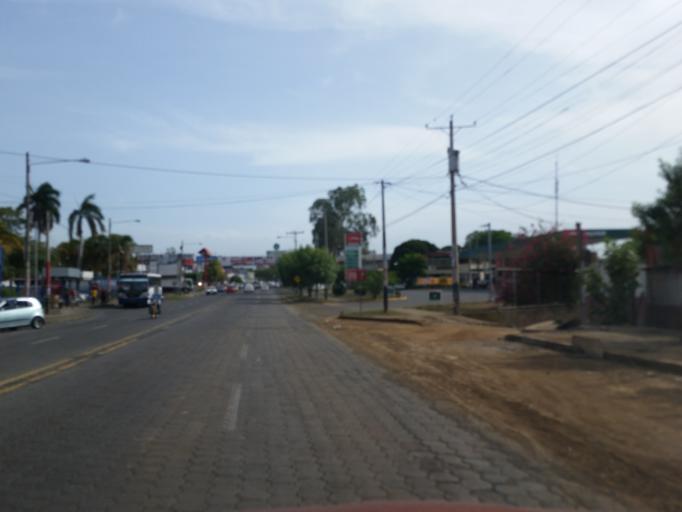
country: NI
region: Managua
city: Managua
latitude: 12.1349
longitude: -86.2549
